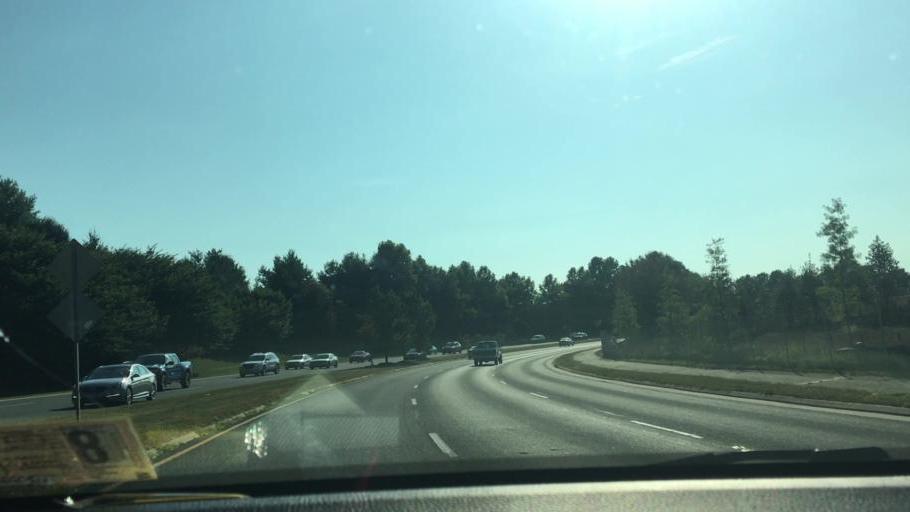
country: US
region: Virginia
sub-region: Prince William County
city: Dale City
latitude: 38.6464
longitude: -77.3091
